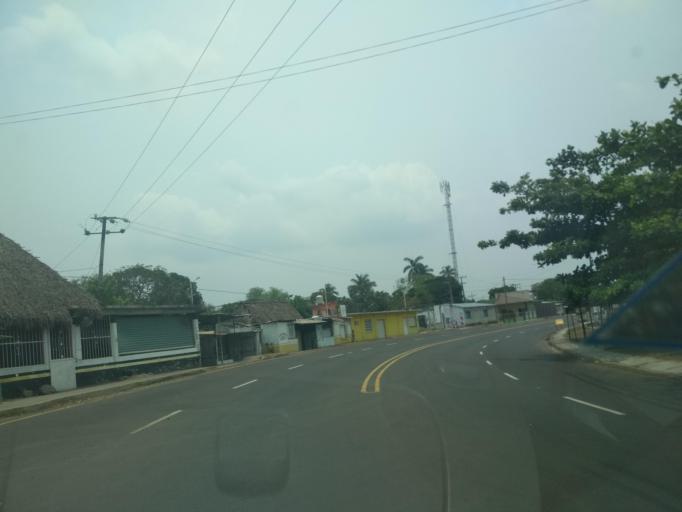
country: MX
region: Veracruz
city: Manlio Fabio Altamirano
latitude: 19.1323
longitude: -96.2976
